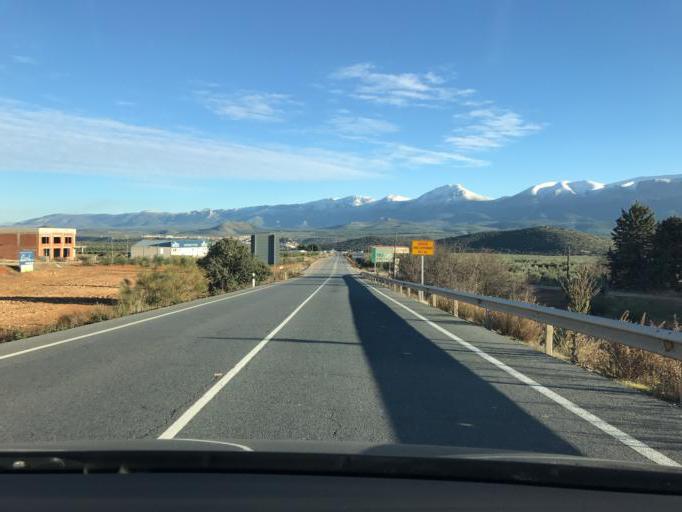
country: ES
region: Andalusia
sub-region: Provincia de Granada
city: Iznalloz
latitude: 37.4045
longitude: -3.5618
